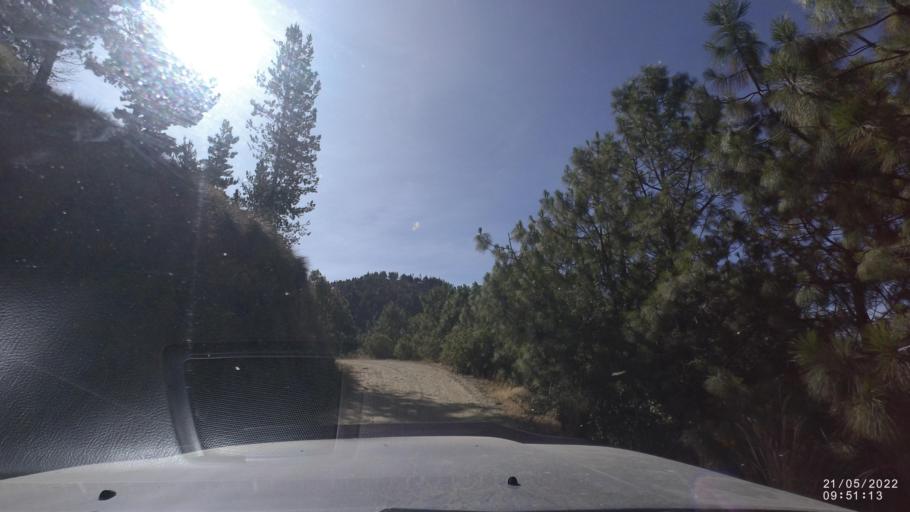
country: BO
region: Cochabamba
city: Colomi
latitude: -17.3424
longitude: -65.9912
